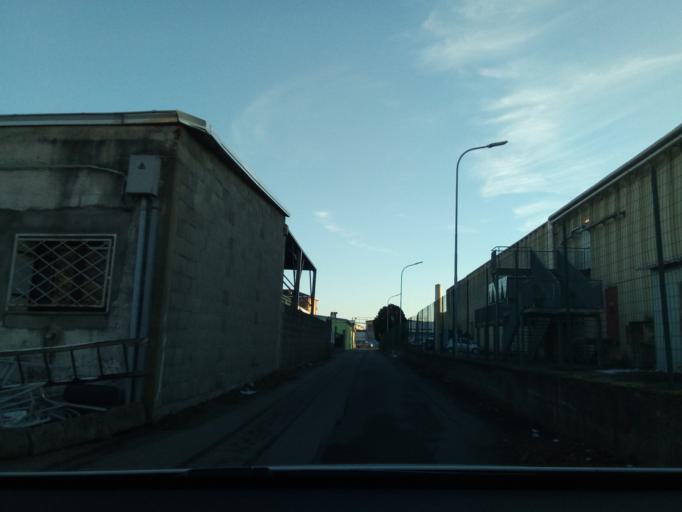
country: IT
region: Piedmont
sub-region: Provincia di Torino
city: Burolo
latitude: 45.4731
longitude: 7.9210
